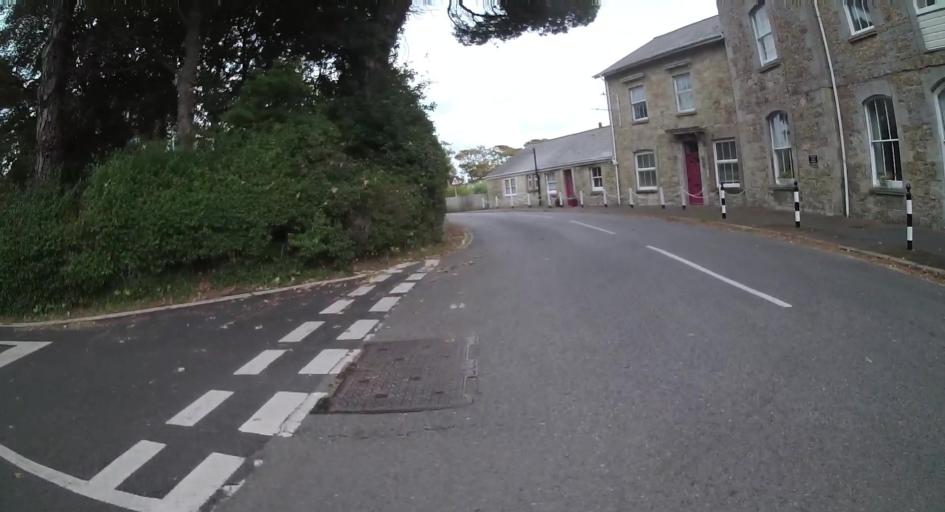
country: GB
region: England
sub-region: Isle of Wight
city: Niton
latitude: 50.5851
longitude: -1.2492
